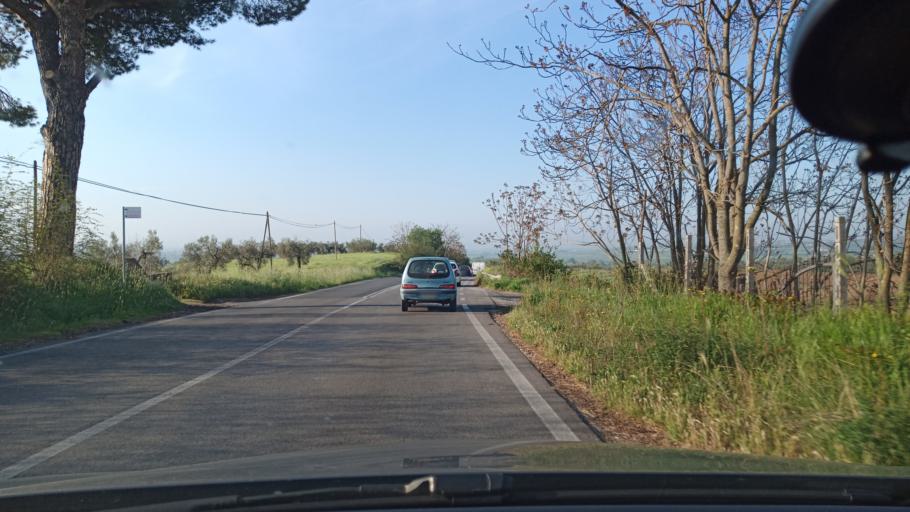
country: IT
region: Latium
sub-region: Citta metropolitana di Roma Capitale
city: Fiano Romano
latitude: 42.1824
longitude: 12.6363
